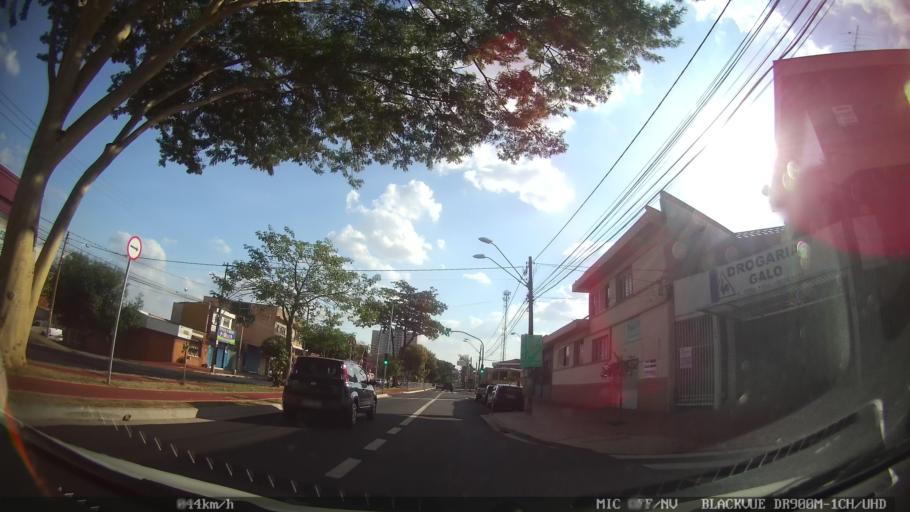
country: BR
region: Sao Paulo
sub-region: Ribeirao Preto
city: Ribeirao Preto
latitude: -21.1749
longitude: -47.8249
